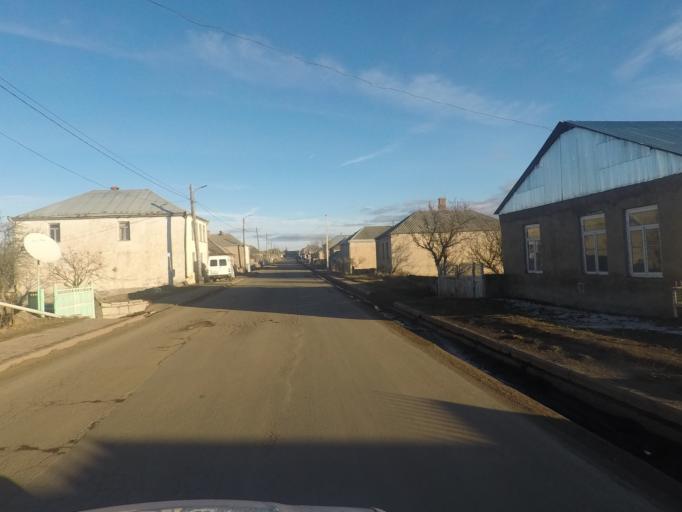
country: GE
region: Kvemo Kartli
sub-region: Tsalka
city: Tsalka
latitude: 41.6049
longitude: 44.0445
